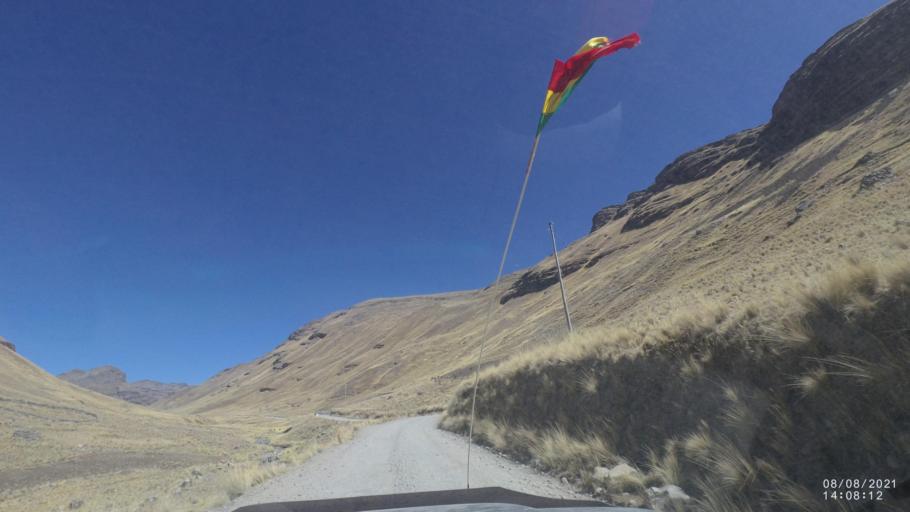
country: BO
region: Cochabamba
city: Sipe Sipe
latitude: -17.1361
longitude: -66.4403
